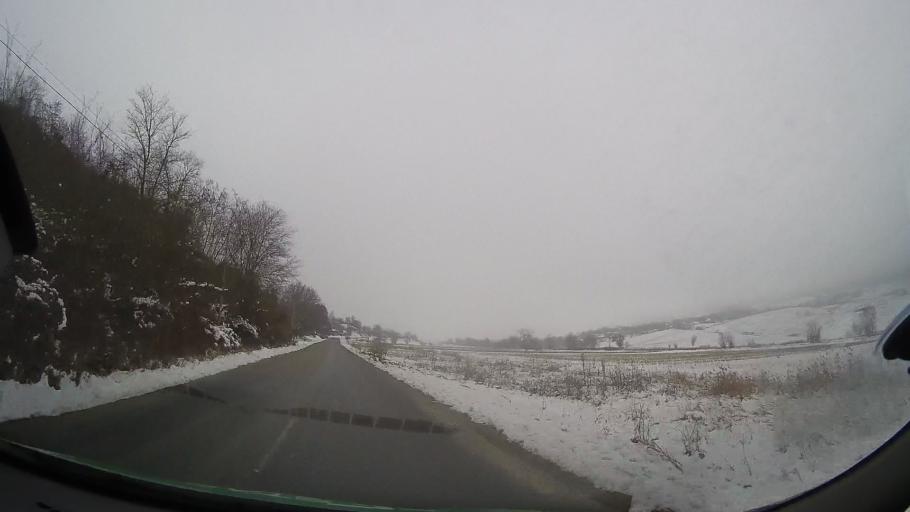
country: RO
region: Bacau
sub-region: Comuna Vultureni
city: Vultureni
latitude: 46.3362
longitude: 27.2908
